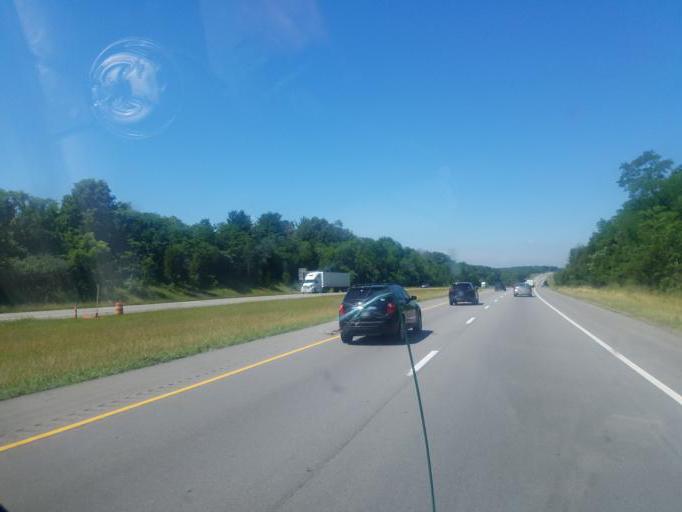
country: US
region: Ohio
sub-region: Warren County
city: Morrow
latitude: 39.4245
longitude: -84.0897
